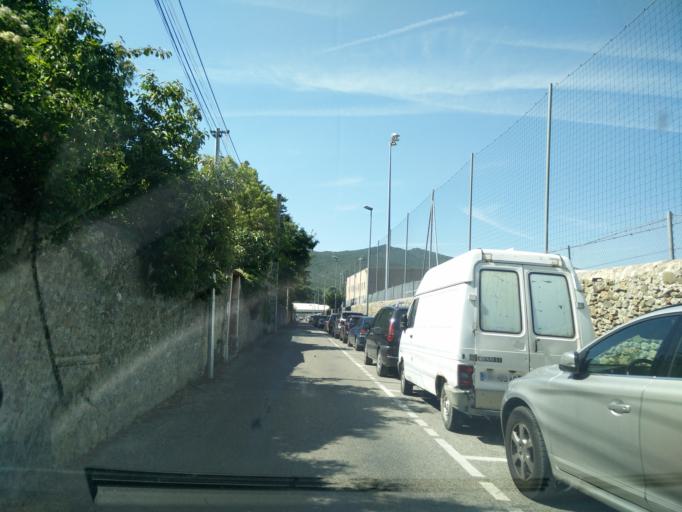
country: FR
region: Rhone-Alpes
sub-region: Departement de la Drome
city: Dieulefit
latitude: 44.5240
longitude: 5.0605
